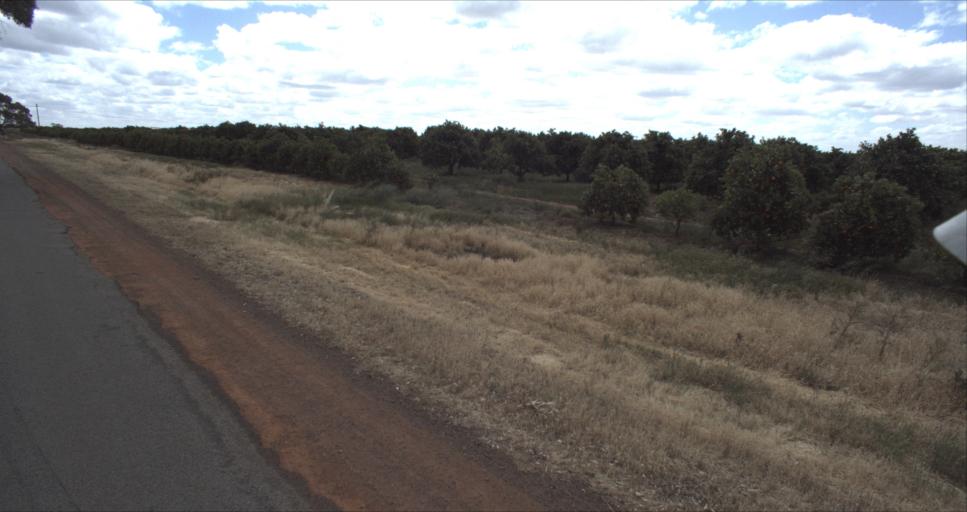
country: AU
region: New South Wales
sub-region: Leeton
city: Leeton
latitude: -34.5889
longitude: 146.3891
